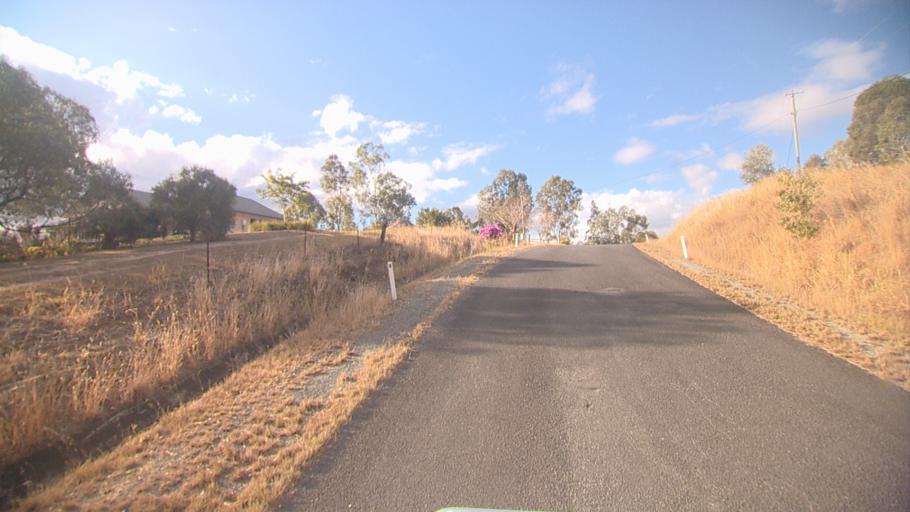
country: AU
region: Queensland
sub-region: Logan
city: Cedar Vale
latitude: -27.9045
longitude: 153.0644
